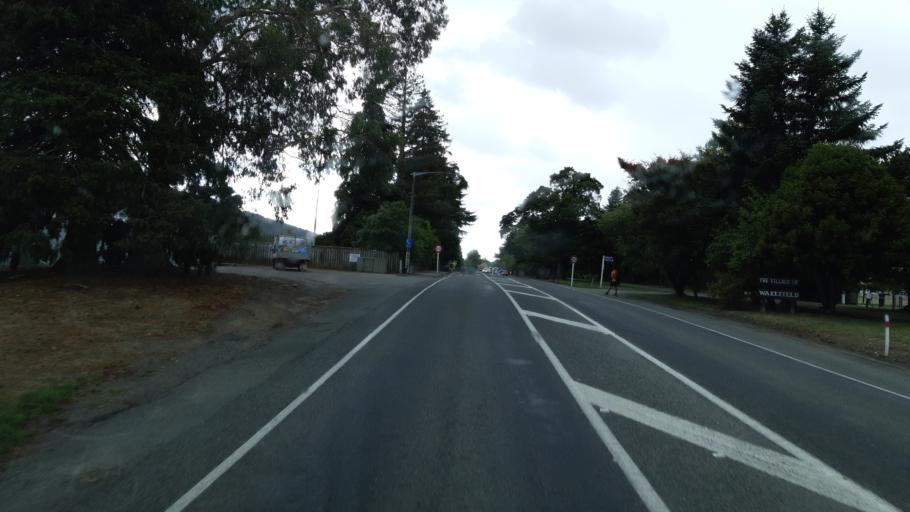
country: NZ
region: Tasman
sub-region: Tasman District
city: Wakefield
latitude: -41.4079
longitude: 173.0388
